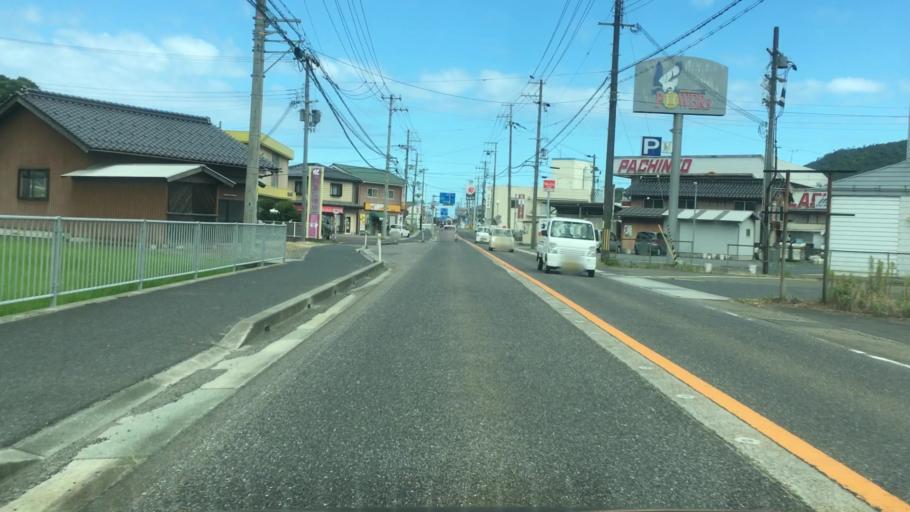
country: JP
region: Tottori
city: Tottori
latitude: 35.6177
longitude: 134.4632
